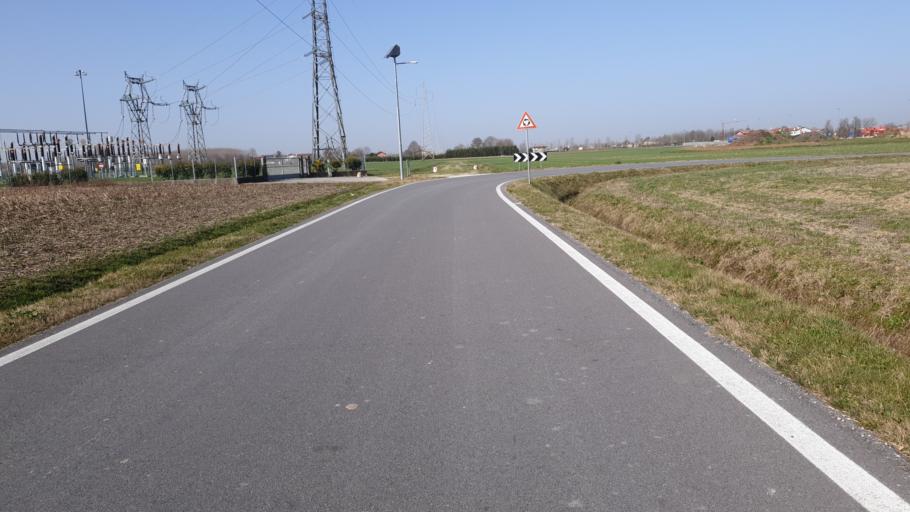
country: IT
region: Veneto
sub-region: Provincia di Padova
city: Cavino
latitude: 45.4938
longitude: 11.8941
